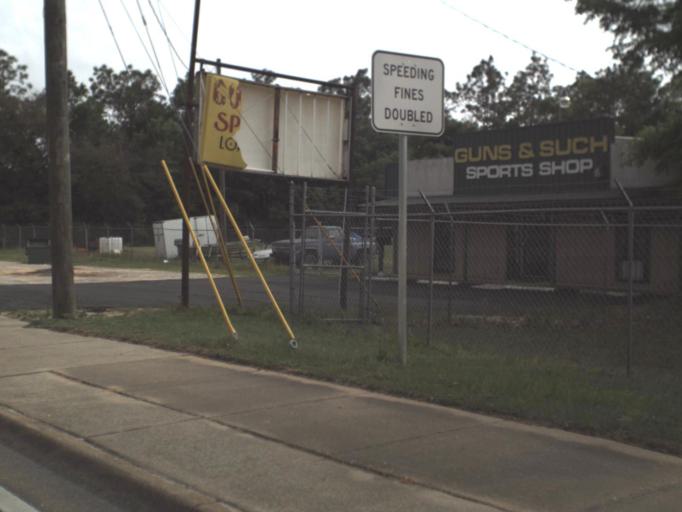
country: US
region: Florida
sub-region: Santa Rosa County
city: Milton
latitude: 30.6512
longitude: -87.0457
